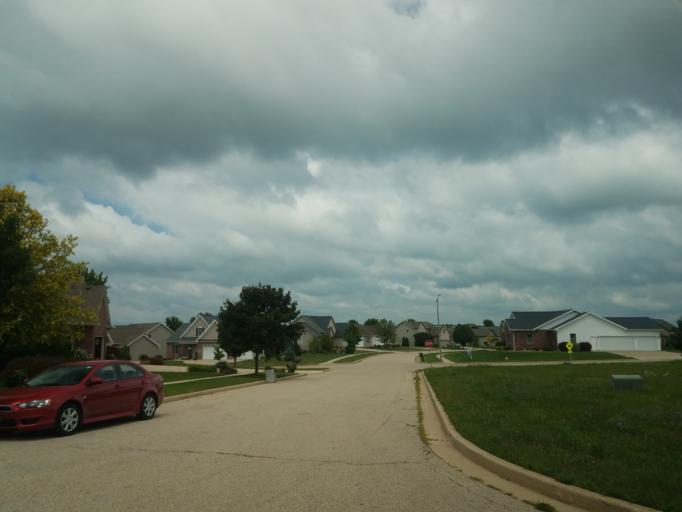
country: US
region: Illinois
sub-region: McLean County
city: Bloomington
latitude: 40.4420
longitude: -89.0370
